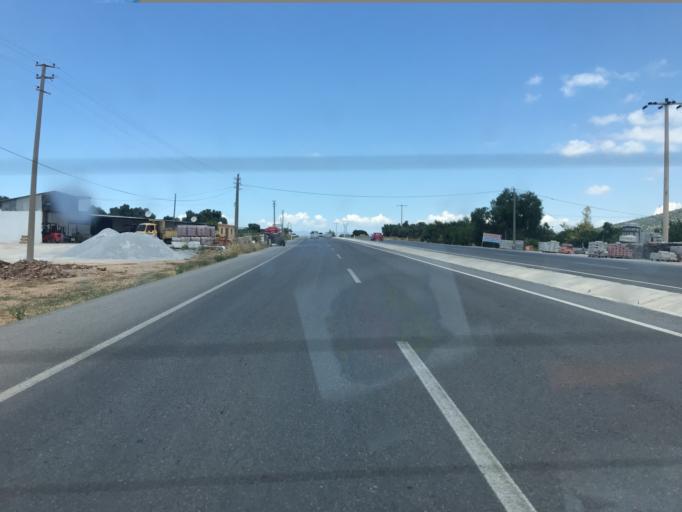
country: TR
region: Aydin
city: Akkoy
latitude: 37.4305
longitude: 27.3670
